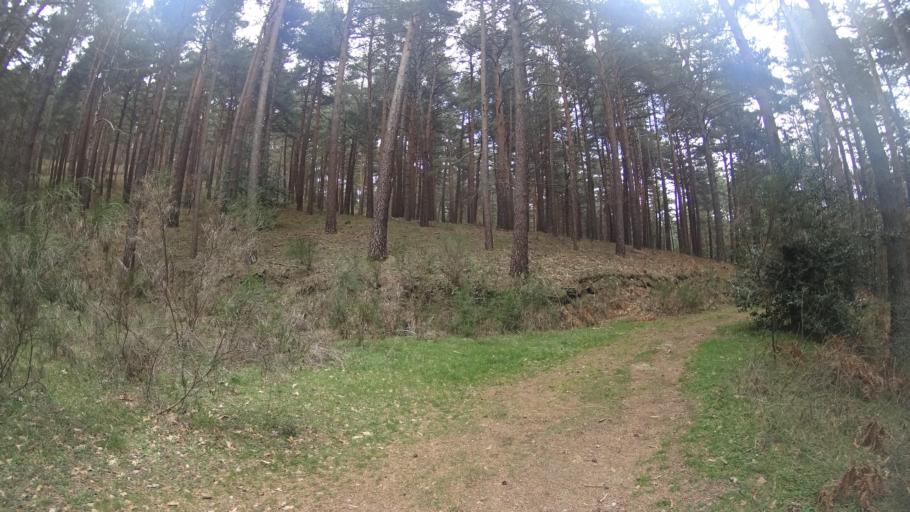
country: ES
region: Madrid
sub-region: Provincia de Madrid
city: Canencia
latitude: 40.8723
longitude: -3.7828
